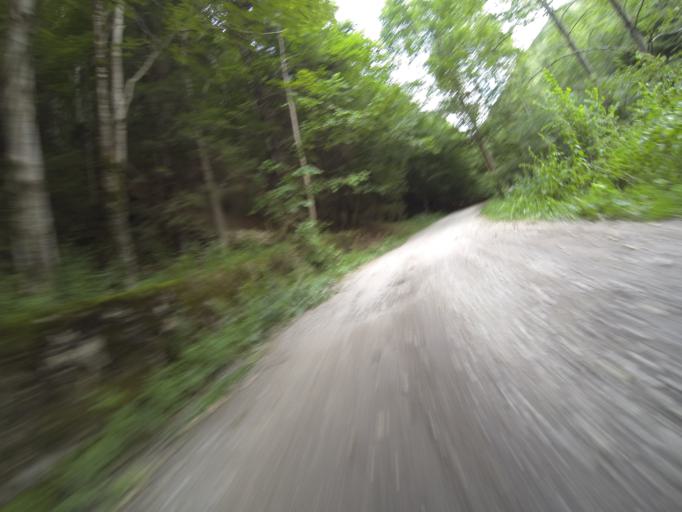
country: RO
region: Gorj
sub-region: Comuna Polovragi
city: Polovragi
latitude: 45.2429
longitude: 23.7667
